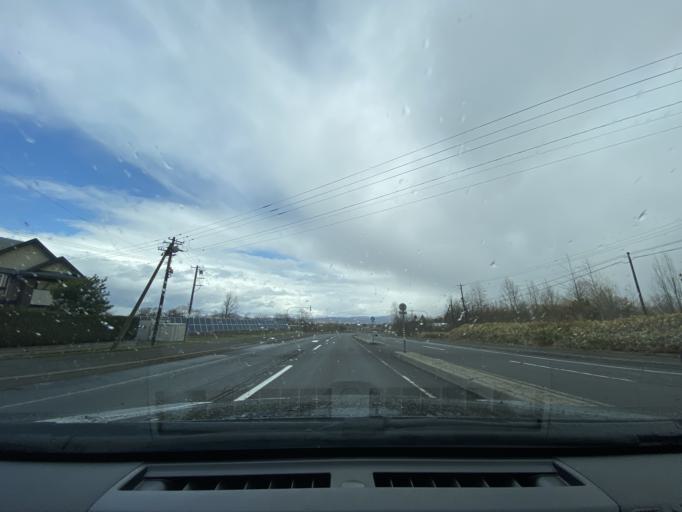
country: JP
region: Hokkaido
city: Fukagawa
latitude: 43.6927
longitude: 142.0573
